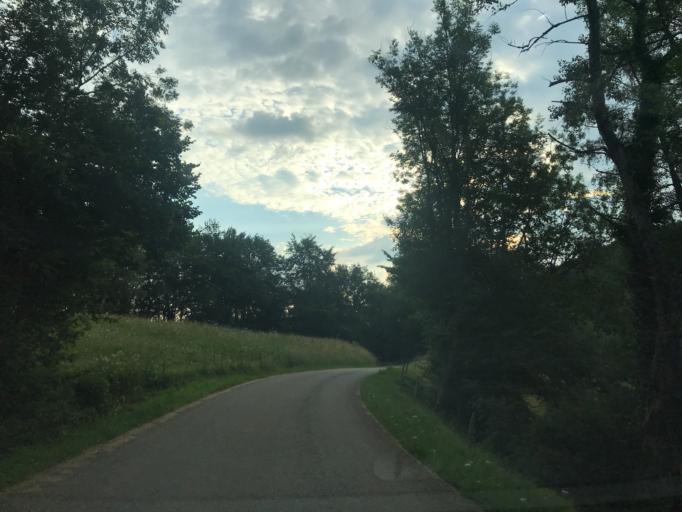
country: FR
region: Rhone-Alpes
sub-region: Departement de l'Isere
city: Saint-Vincent-de-Mercuze
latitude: 45.3812
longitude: 5.9288
